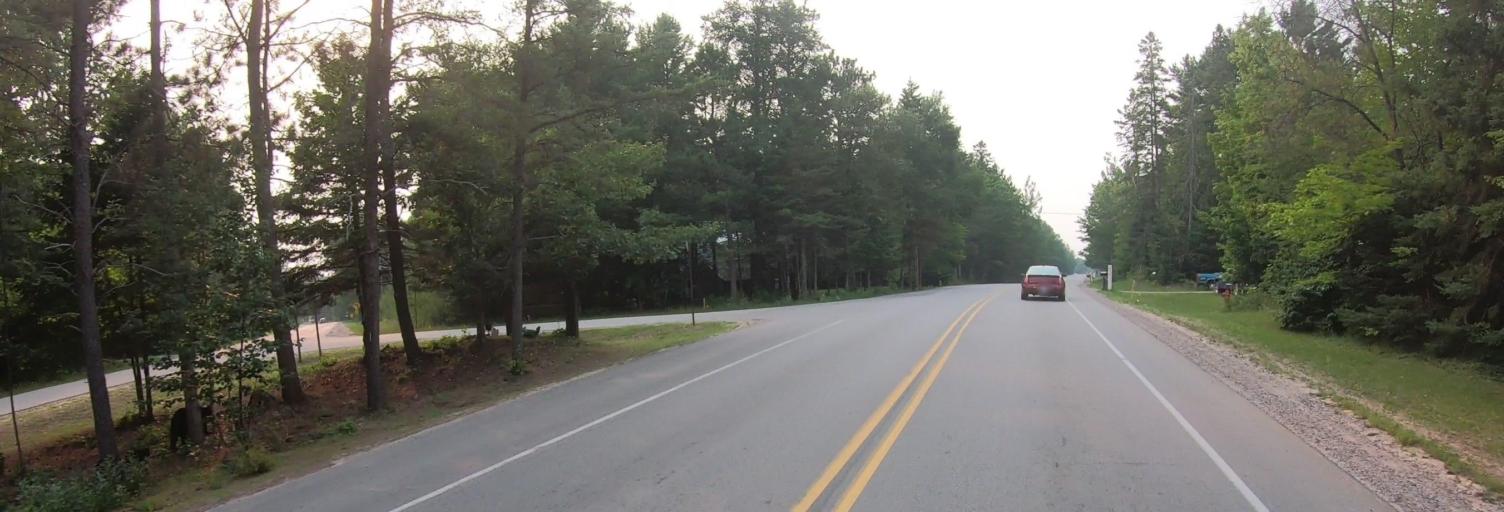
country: US
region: Michigan
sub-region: Chippewa County
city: Sault Ste. Marie
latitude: 46.4571
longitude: -84.6138
